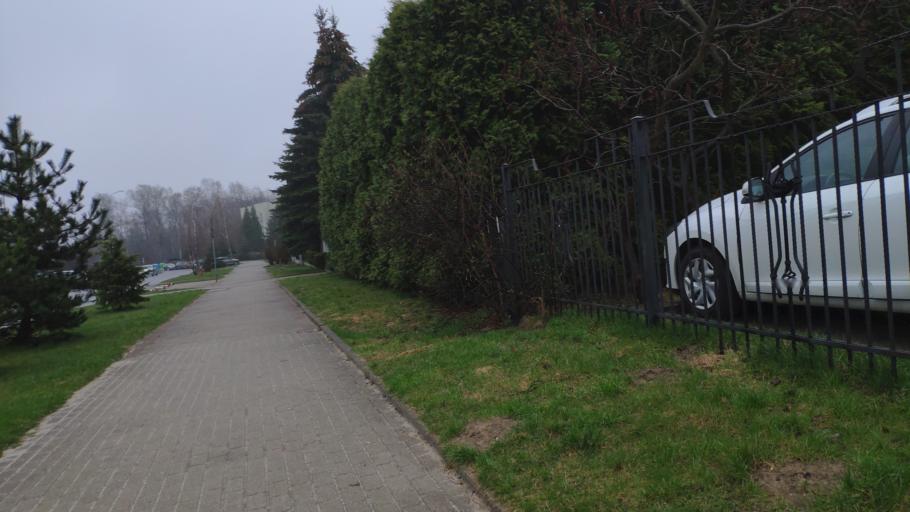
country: PL
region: Lodz Voivodeship
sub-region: Powiat lodzki wschodni
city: Andrespol
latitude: 51.7525
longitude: 19.5679
